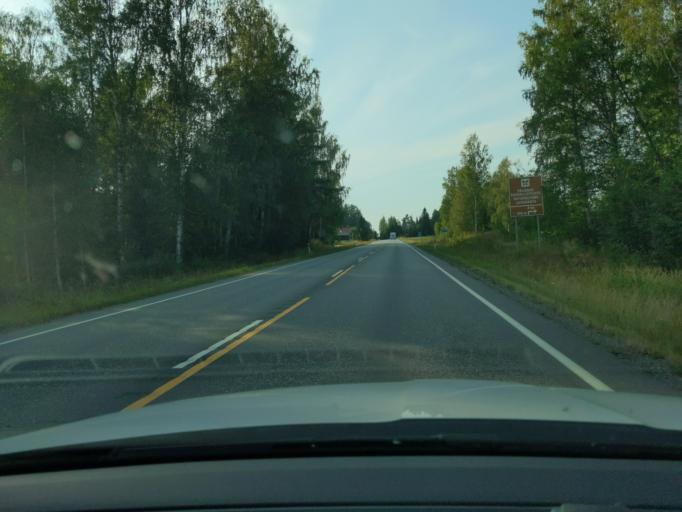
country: FI
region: Paijanne Tavastia
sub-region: Lahti
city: Padasjoki
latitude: 61.3382
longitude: 25.2608
